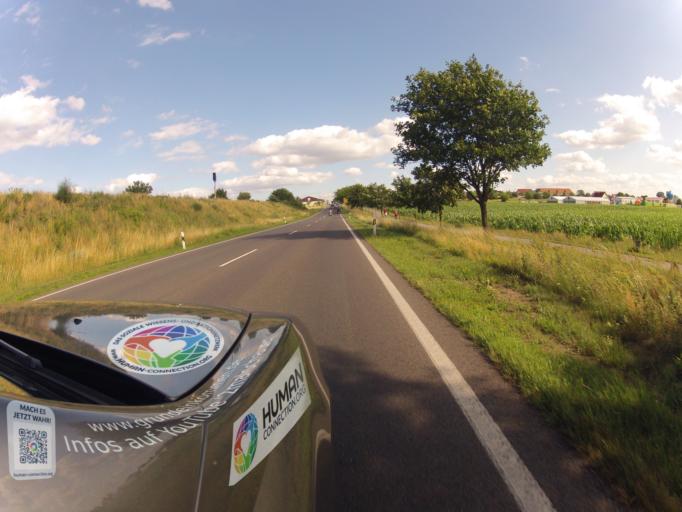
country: DE
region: Mecklenburg-Vorpommern
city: Loddin
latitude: 54.0172
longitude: 14.0442
